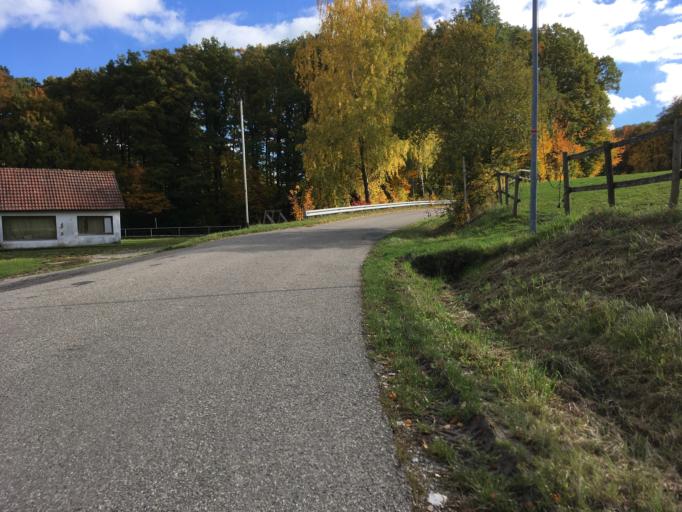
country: DE
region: Baden-Wuerttemberg
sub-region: Regierungsbezirk Stuttgart
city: Waldenburg
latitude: 49.1878
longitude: 9.6688
